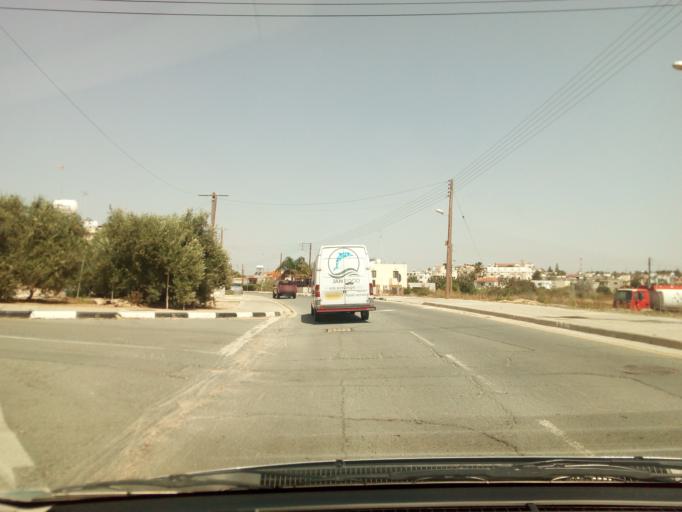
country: CY
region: Larnaka
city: Xylotymbou
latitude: 34.9882
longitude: 33.7810
